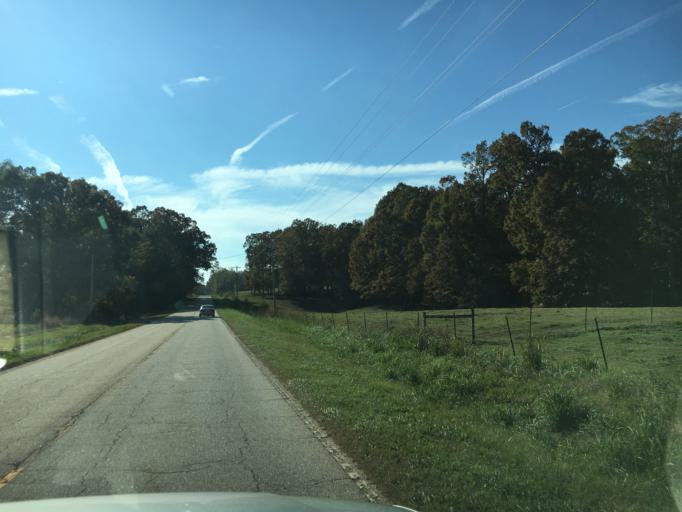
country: US
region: South Carolina
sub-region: Anderson County
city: Iva
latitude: 34.3443
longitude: -82.7480
